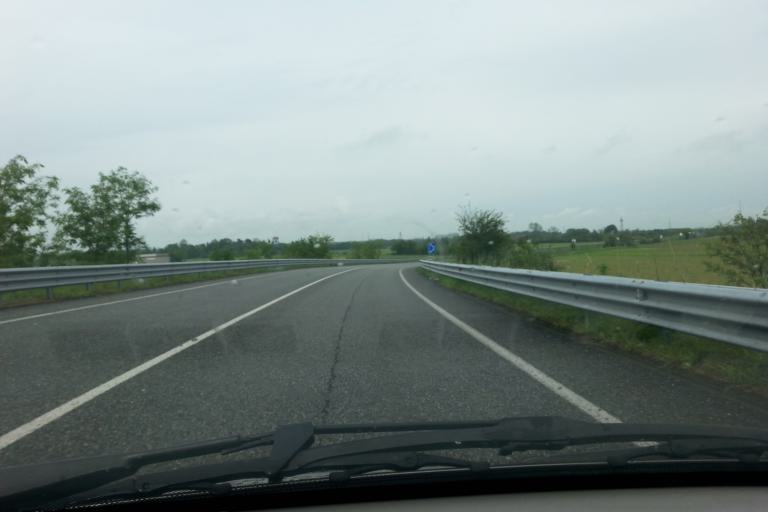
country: IT
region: Piedmont
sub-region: Provincia di Torino
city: Alpignano
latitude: 45.1196
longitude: 7.5180
